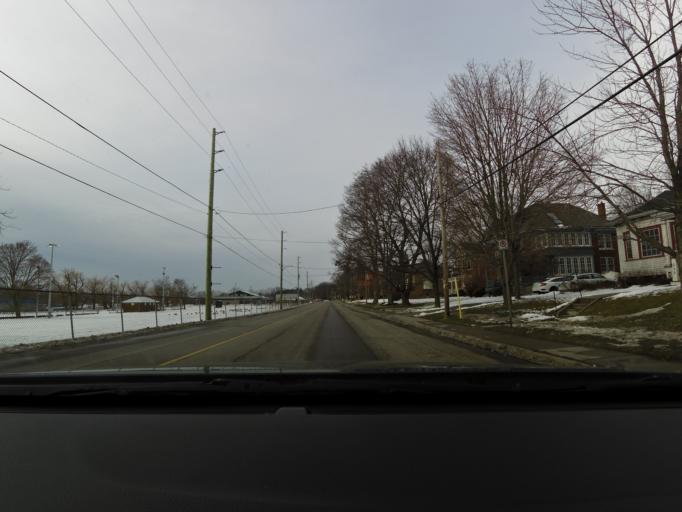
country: CA
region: Ontario
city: Ancaster
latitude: 43.0713
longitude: -79.9440
